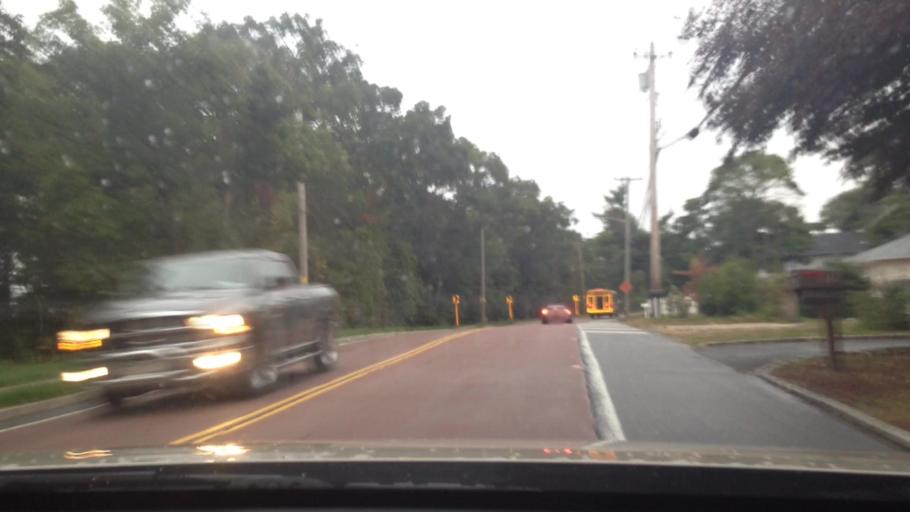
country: US
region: New York
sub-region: Suffolk County
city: Farmingville
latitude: 40.8425
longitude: -73.0550
